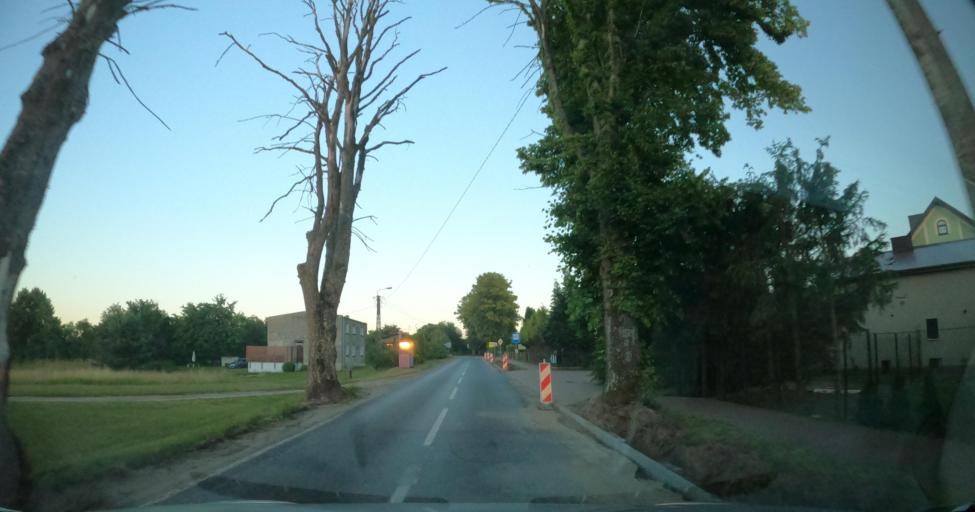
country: PL
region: Pomeranian Voivodeship
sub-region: Powiat wejherowski
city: Linia
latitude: 54.4521
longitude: 17.9257
